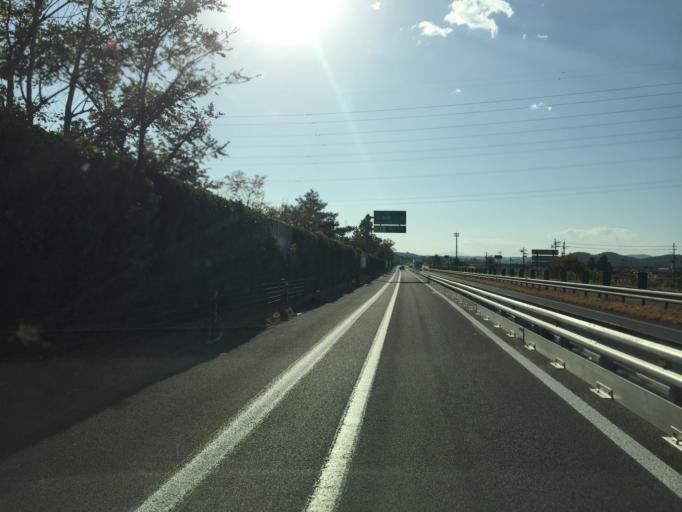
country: JP
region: Fukushima
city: Fukushima-shi
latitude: 37.7466
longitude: 140.4136
